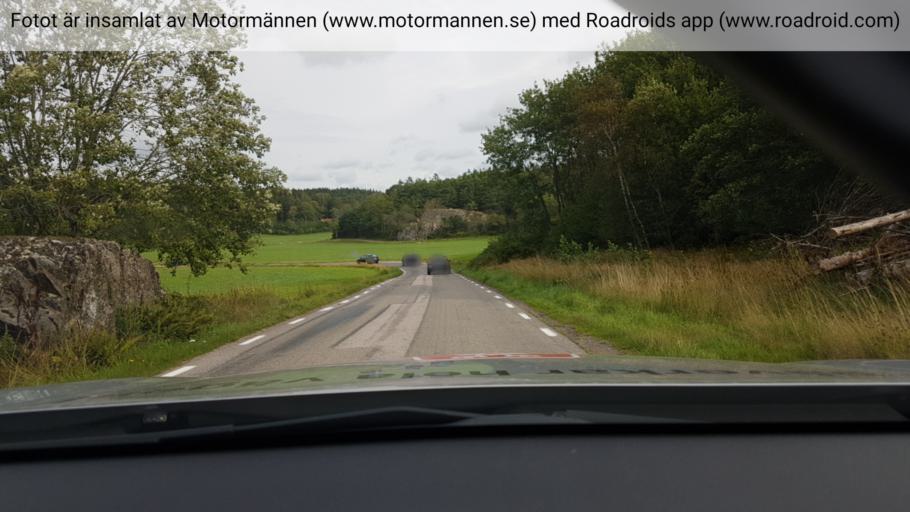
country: SE
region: Vaestra Goetaland
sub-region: Orust
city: Henan
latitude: 58.2453
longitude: 11.5546
